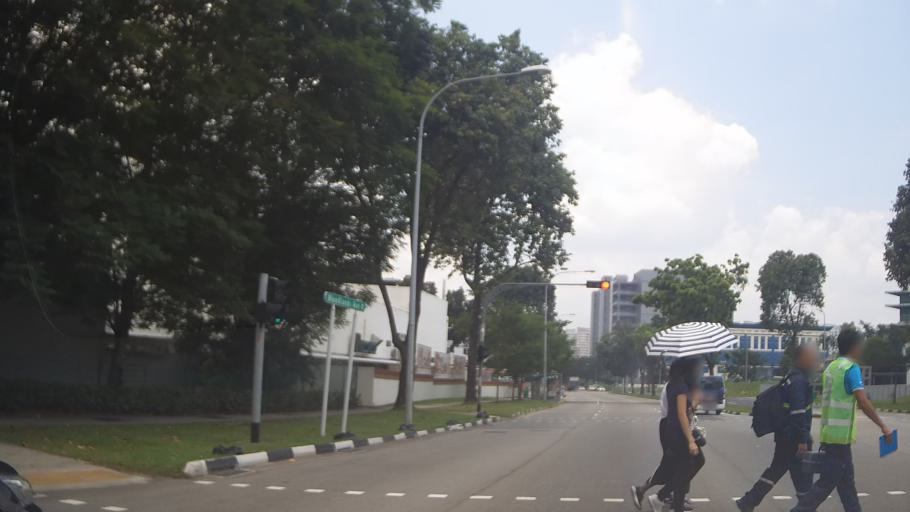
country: MY
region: Johor
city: Johor Bahru
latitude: 1.4556
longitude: 103.8008
